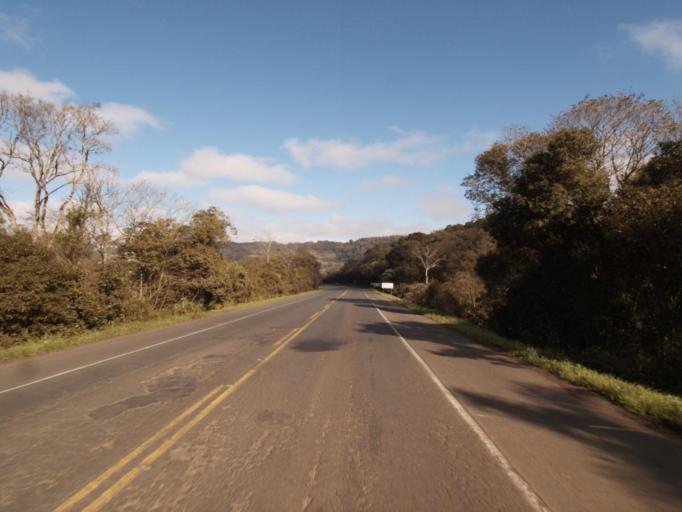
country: BR
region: Rio Grande do Sul
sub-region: Frederico Westphalen
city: Frederico Westphalen
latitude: -27.0666
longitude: -53.2256
